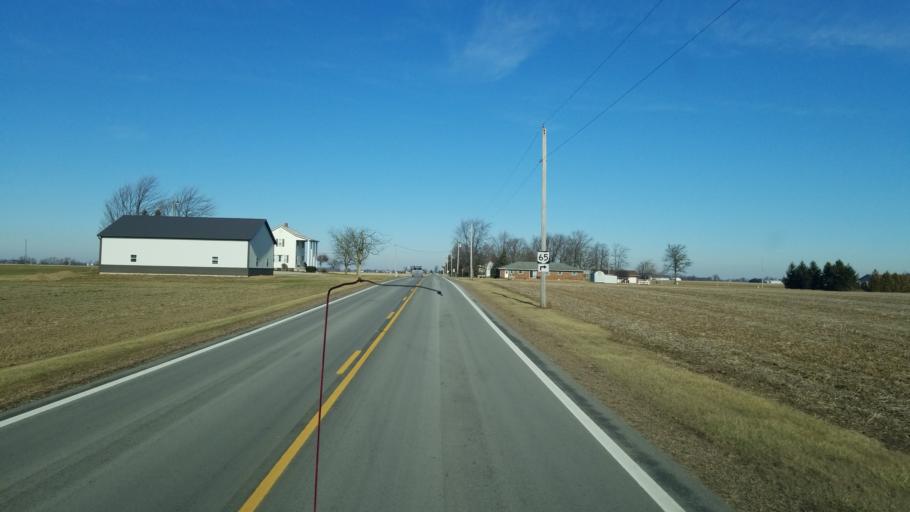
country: US
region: Ohio
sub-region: Putnam County
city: Leipsic
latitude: 41.1214
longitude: -83.9770
